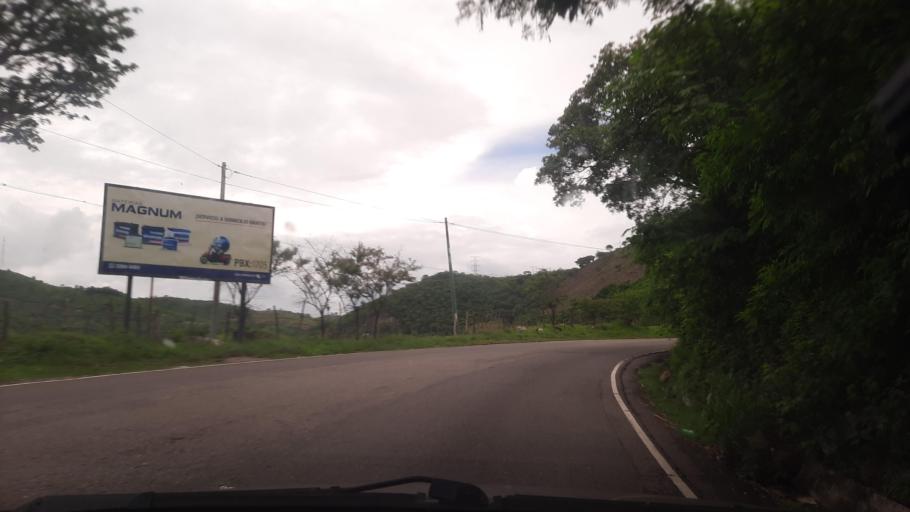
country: GT
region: Chiquimula
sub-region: Municipio de Chiquimula
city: Chiquimula
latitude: 14.8736
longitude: -89.5119
